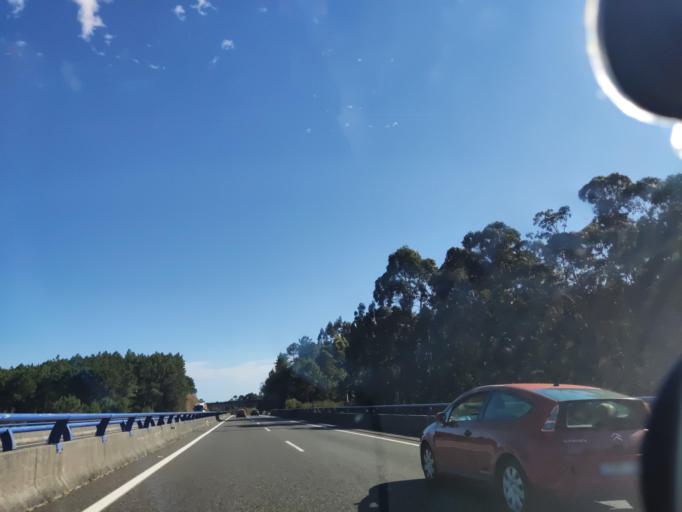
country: ES
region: Galicia
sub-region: Provincia da Coruna
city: Boiro
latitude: 42.6410
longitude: -8.9114
